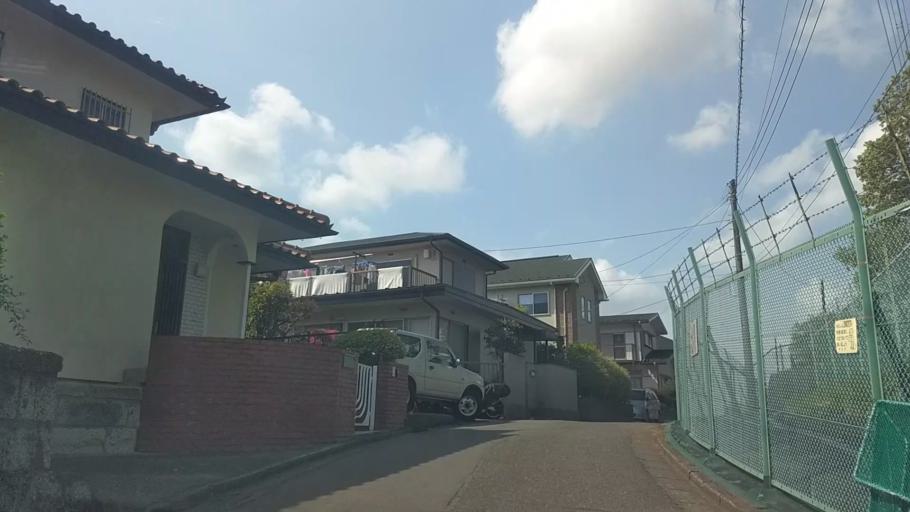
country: JP
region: Kanagawa
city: Kamakura
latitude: 35.3793
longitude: 139.5669
